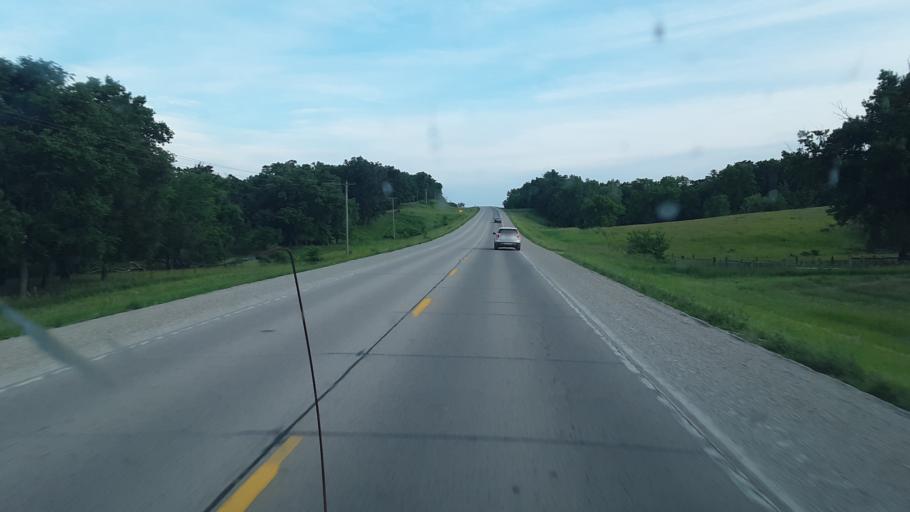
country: US
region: Iowa
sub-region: Benton County
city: Belle Plaine
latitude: 41.8411
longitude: -92.2787
